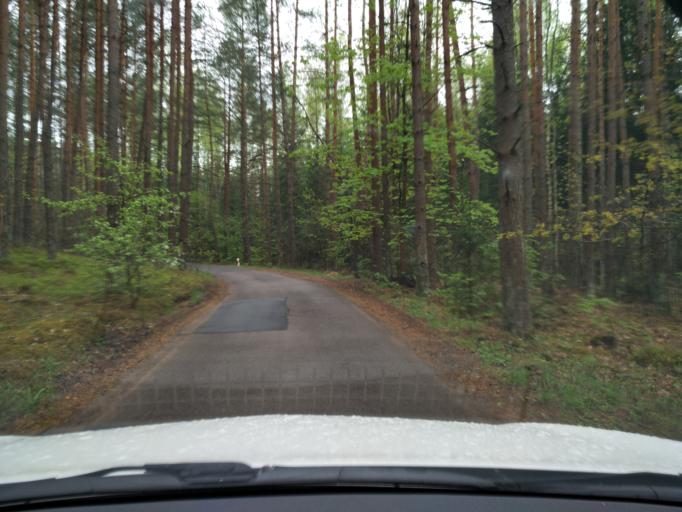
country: LT
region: Vilnius County
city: Rasos
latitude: 54.7405
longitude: 25.3980
